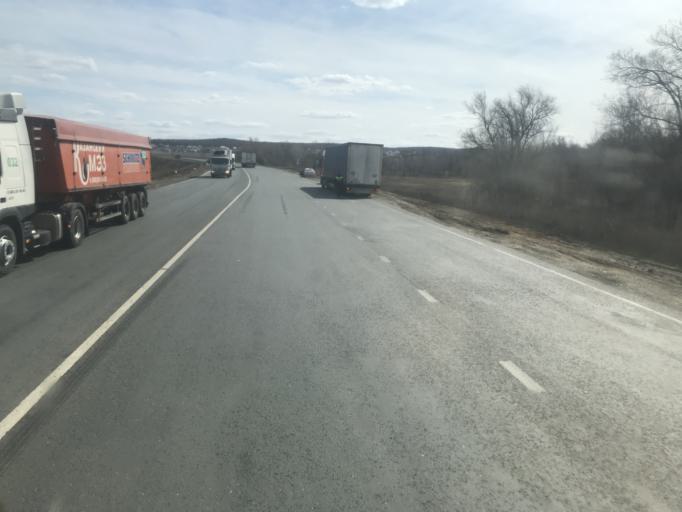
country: RU
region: Samara
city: Novosemeykino
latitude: 53.4114
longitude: 50.3500
